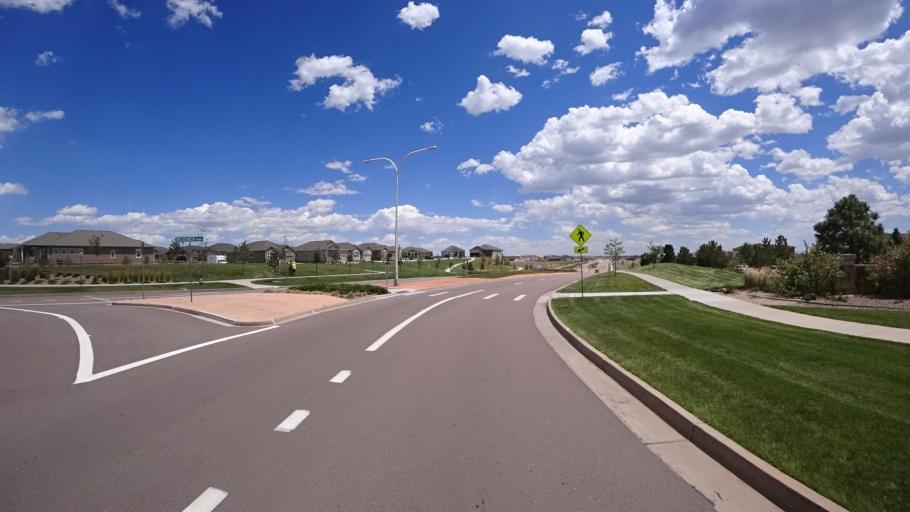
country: US
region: Colorado
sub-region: El Paso County
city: Black Forest
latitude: 38.9618
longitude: -104.7142
